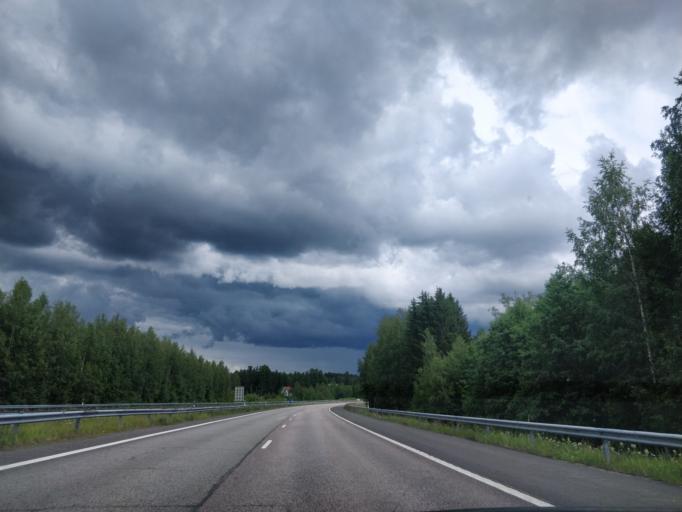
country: FI
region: Paijanne Tavastia
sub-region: Lahti
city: Heinola
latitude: 61.2990
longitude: 26.0836
